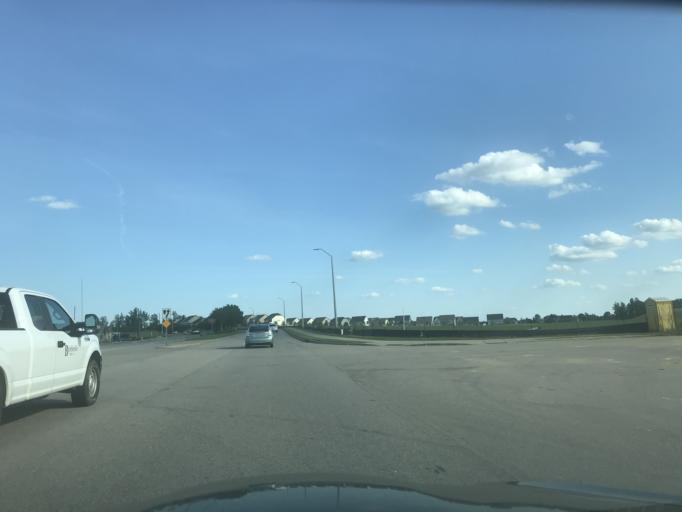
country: US
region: North Carolina
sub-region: Wake County
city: Knightdale
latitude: 35.7766
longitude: -78.4337
